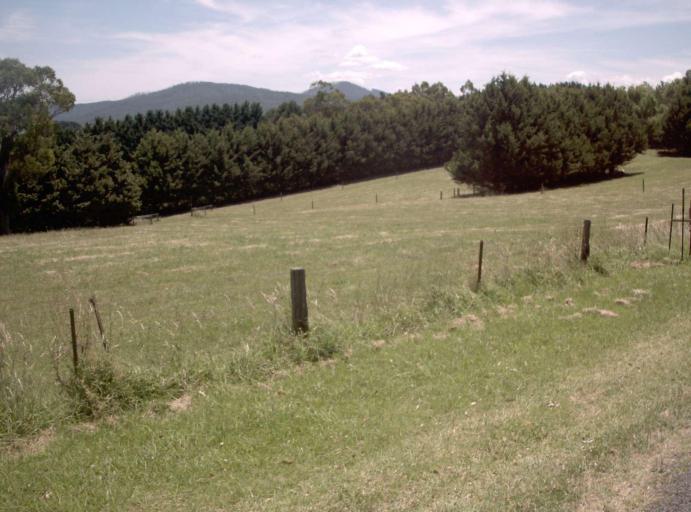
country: AU
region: Victoria
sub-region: Baw Baw
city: Warragul
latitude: -38.0034
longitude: 145.9539
